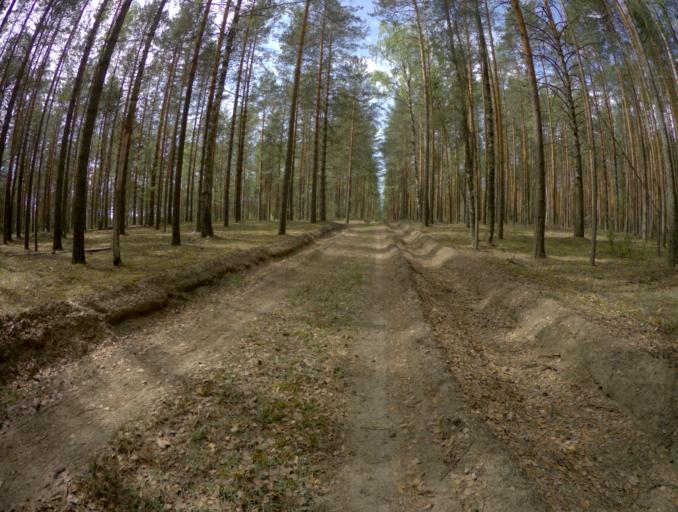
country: RU
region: Ivanovo
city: Talitsy
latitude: 56.4865
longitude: 42.1657
